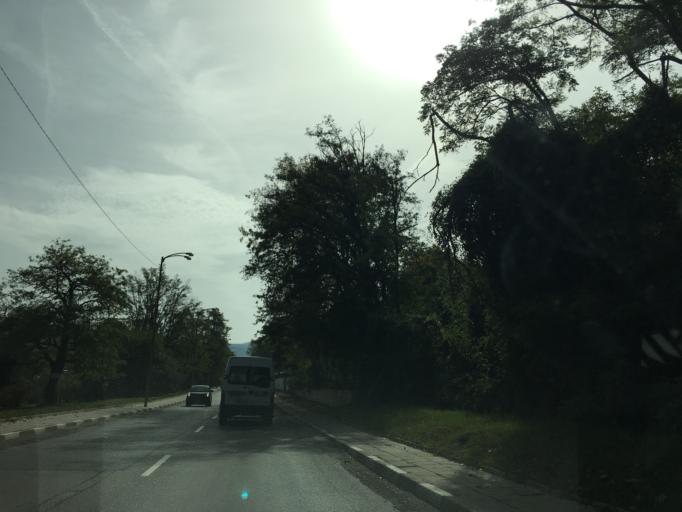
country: BG
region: Sofia-Capital
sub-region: Stolichna Obshtina
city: Sofia
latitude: 42.5902
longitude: 23.4186
